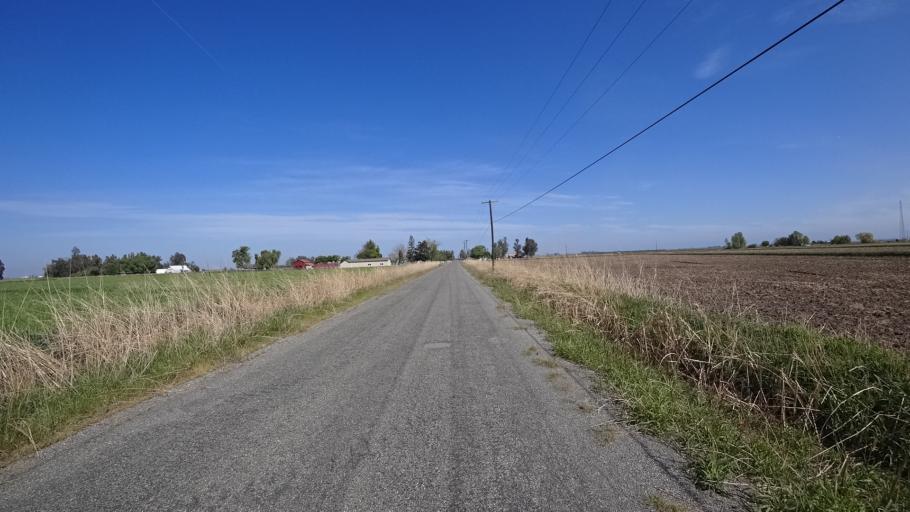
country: US
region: California
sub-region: Glenn County
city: Willows
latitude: 39.5918
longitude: -122.0558
